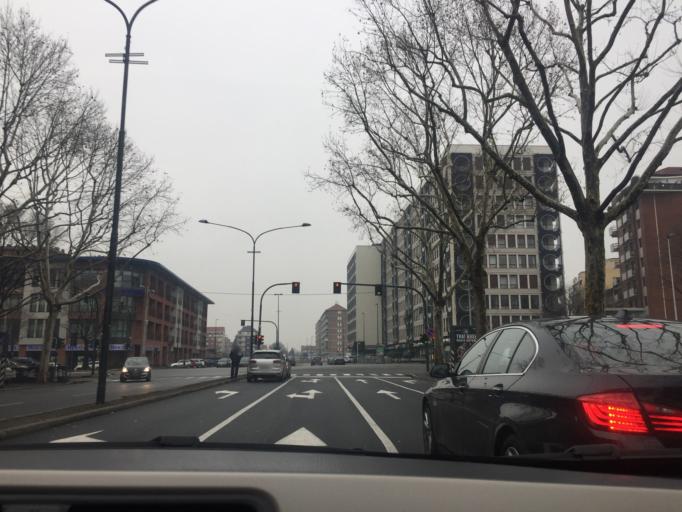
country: IT
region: Piedmont
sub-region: Provincia di Torino
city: Lesna
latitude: 45.0751
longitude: 7.6145
